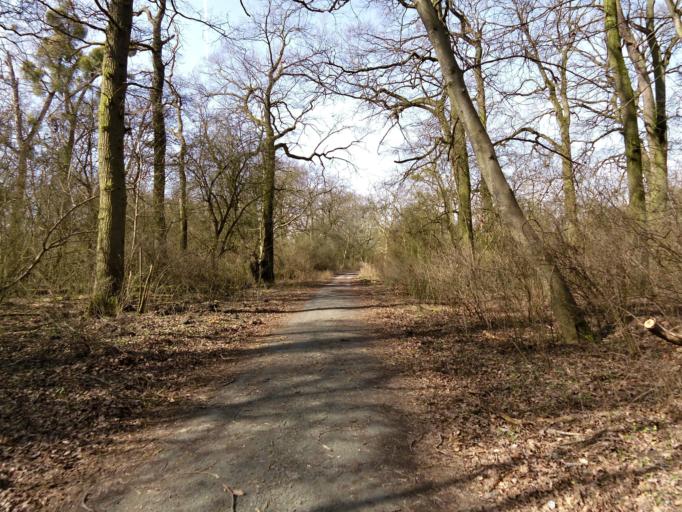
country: DE
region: Rheinland-Pfalz
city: Gimbsheim
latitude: 49.8076
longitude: 8.4021
